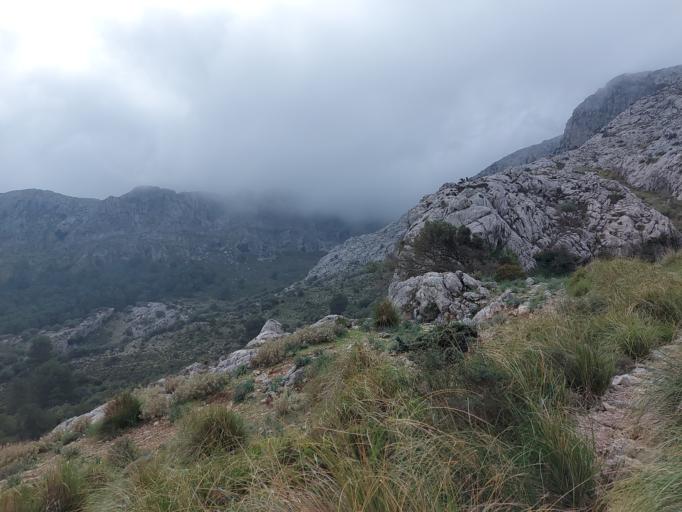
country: ES
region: Balearic Islands
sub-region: Illes Balears
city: Fornalutx
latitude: 39.7583
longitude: 2.7504
